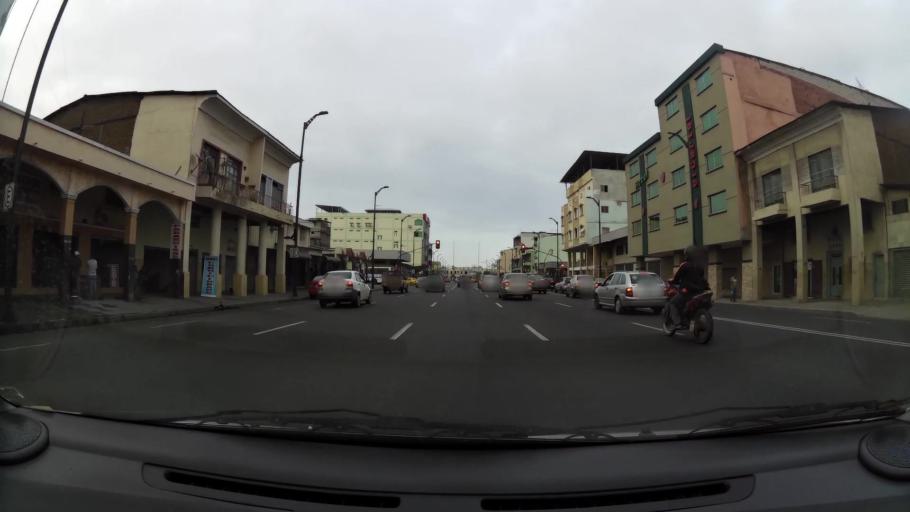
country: EC
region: Guayas
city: Guayaquil
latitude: -2.1991
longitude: -79.8930
